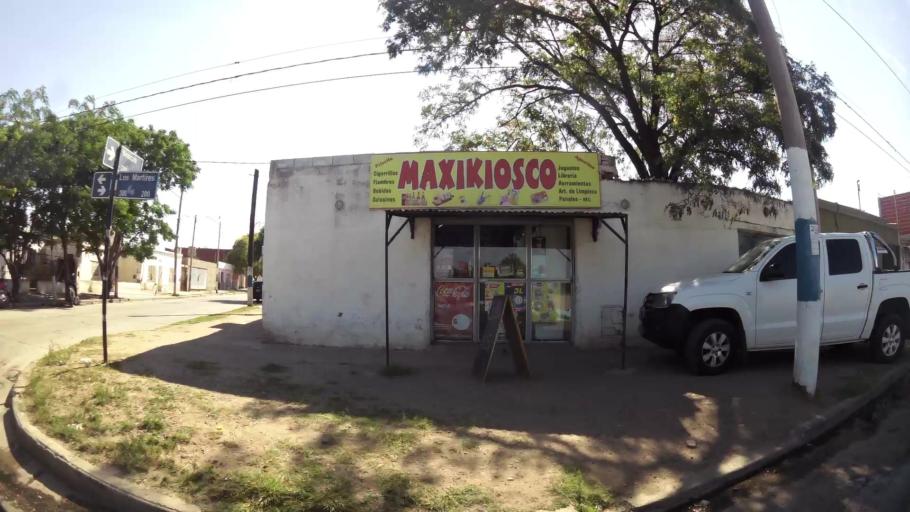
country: AR
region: Cordoba
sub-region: Departamento de Capital
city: Cordoba
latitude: -31.4144
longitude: -64.1480
